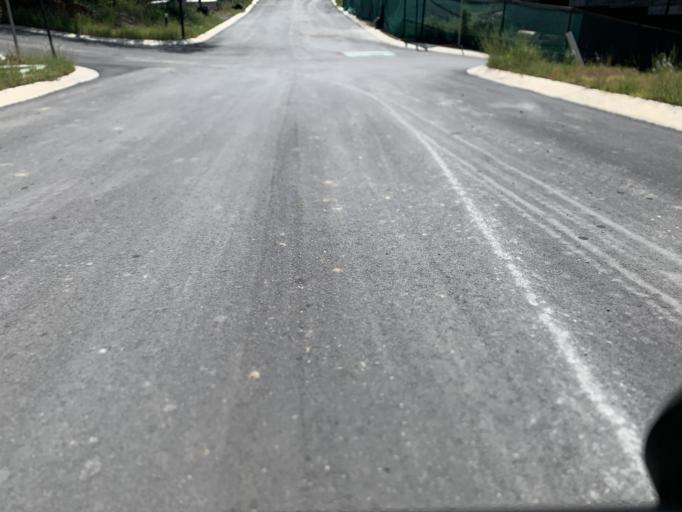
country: MX
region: Nuevo Leon
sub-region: Juarez
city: Bosques de San Pedro
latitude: 25.5250
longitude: -100.1924
